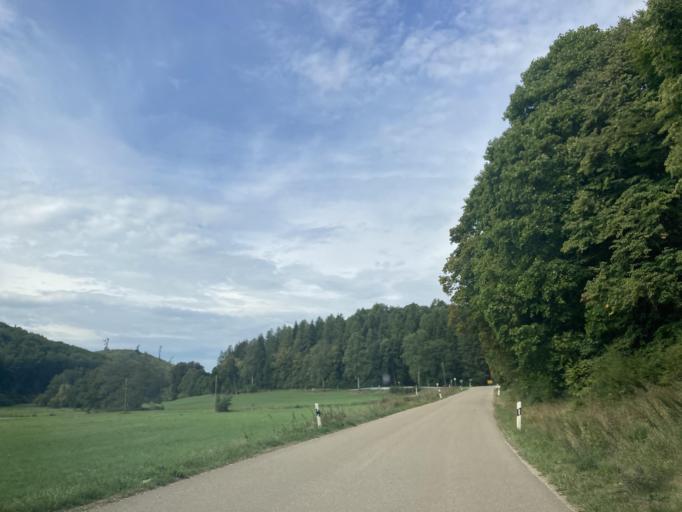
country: DE
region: Bavaria
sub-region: Swabia
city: Ederheim
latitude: 48.7870
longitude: 10.4810
